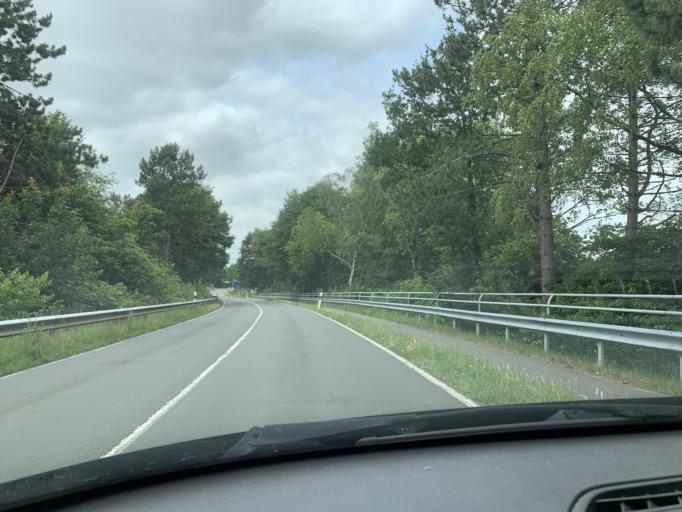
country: DE
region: Lower Saxony
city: Westerstede
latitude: 53.2531
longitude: 7.9679
